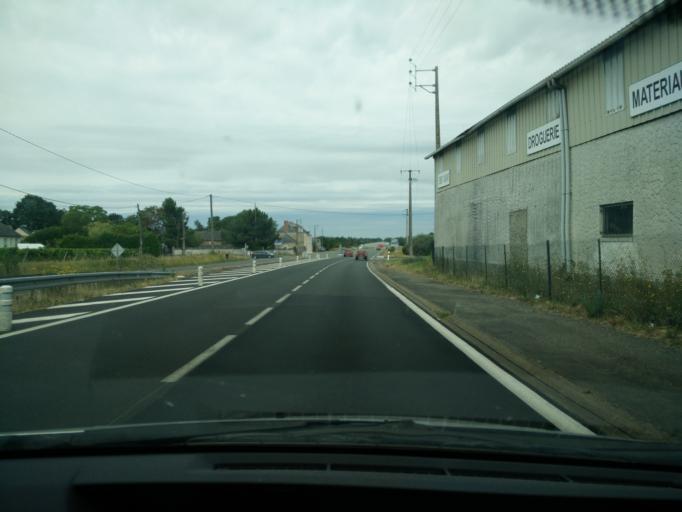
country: FR
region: Pays de la Loire
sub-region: Departement de Maine-et-Loire
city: Saint-Melaine-sur-Aubance
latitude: 47.3875
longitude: -0.4922
